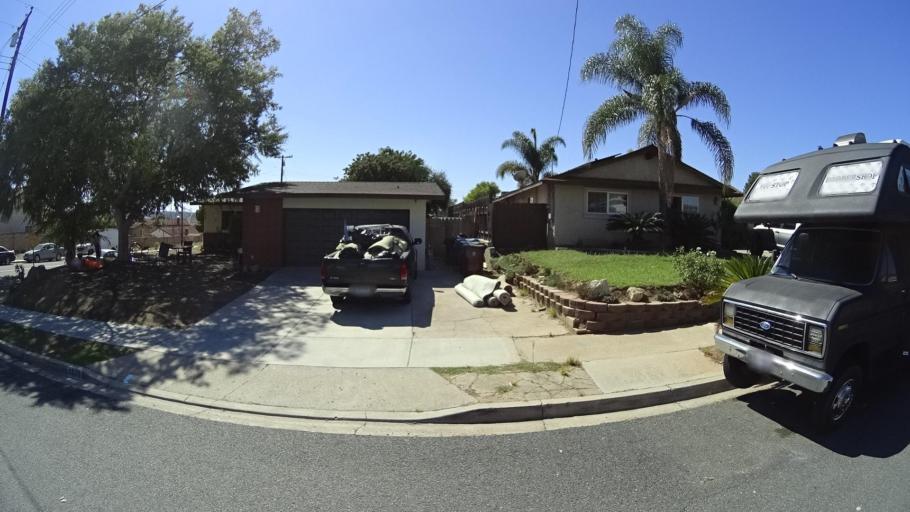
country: US
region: California
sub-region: San Diego County
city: La Presa
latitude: 32.6972
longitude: -117.0066
